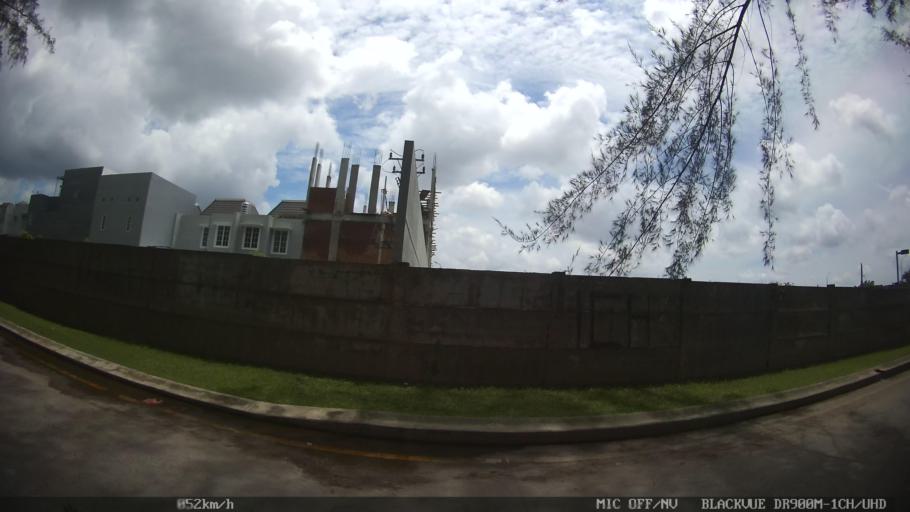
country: ID
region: North Sumatra
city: Medan
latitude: 3.6093
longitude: 98.7295
